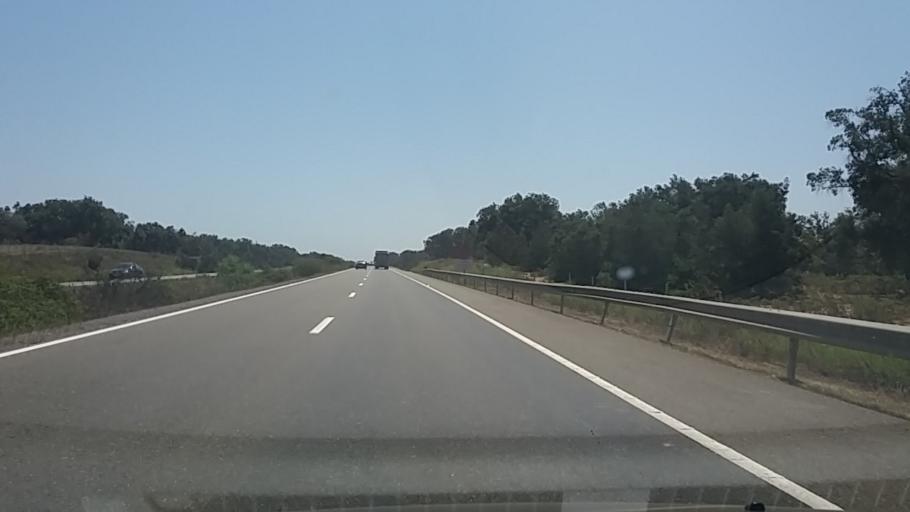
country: MA
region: Gharb-Chrarda-Beni Hssen
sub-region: Kenitra Province
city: Kenitra
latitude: 34.1549
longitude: -6.6777
